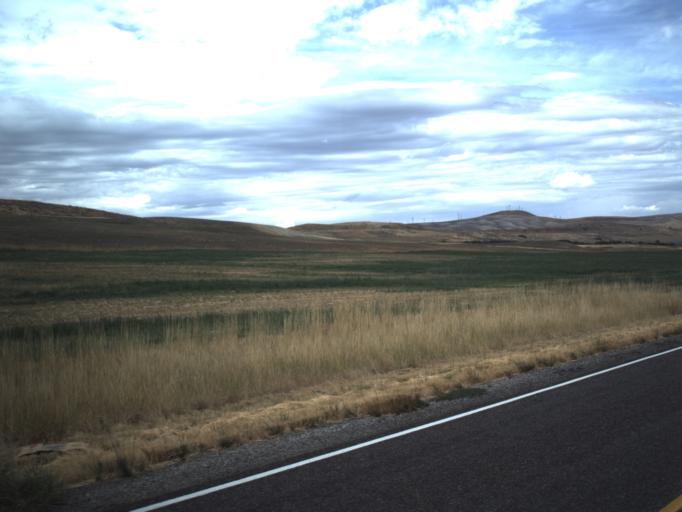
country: US
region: Utah
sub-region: Cache County
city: Lewiston
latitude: 41.9069
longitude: -111.9523
